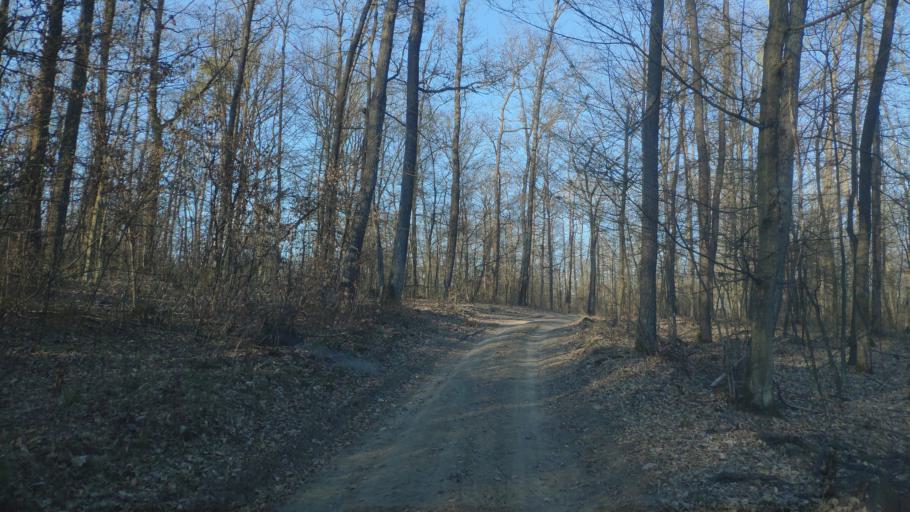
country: HU
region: Borsod-Abauj-Zemplen
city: Putnok
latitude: 48.5043
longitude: 20.3054
